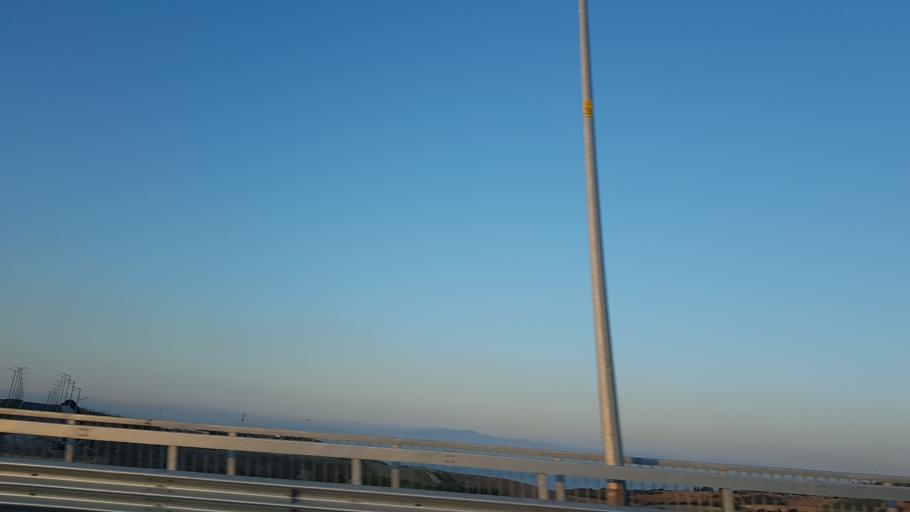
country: TR
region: Kocaeli
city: Tavsanli
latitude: 40.7941
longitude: 29.5092
